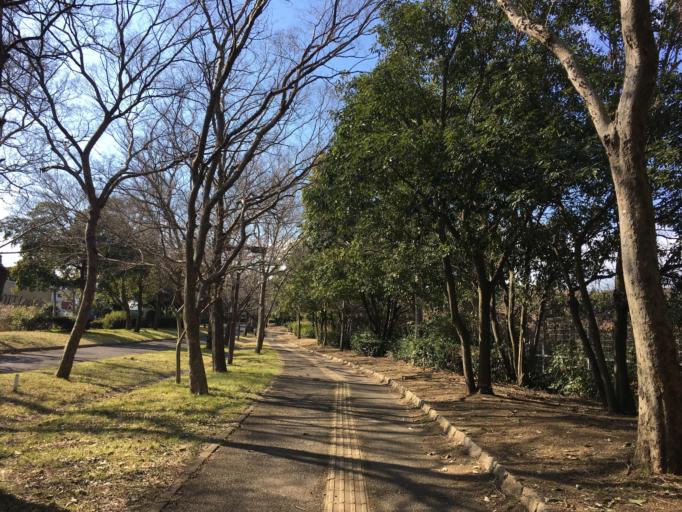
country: JP
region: Hyogo
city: Amagasaki
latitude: 34.6374
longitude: 135.4048
